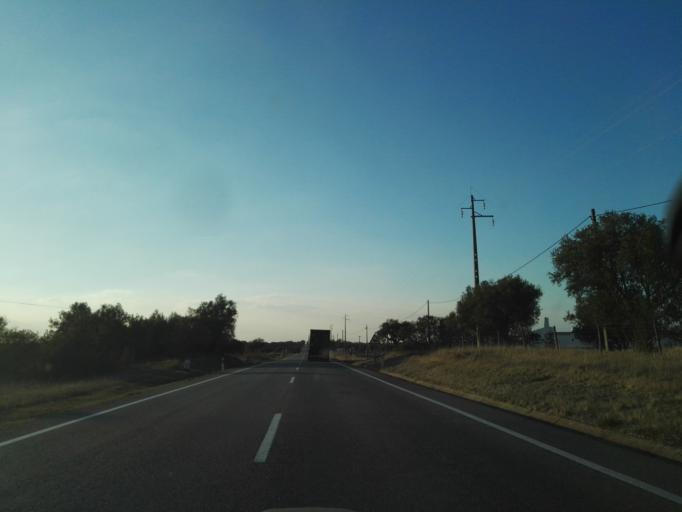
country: PT
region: Evora
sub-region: Arraiolos
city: Arraiolos
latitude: 38.8385
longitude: -7.8620
